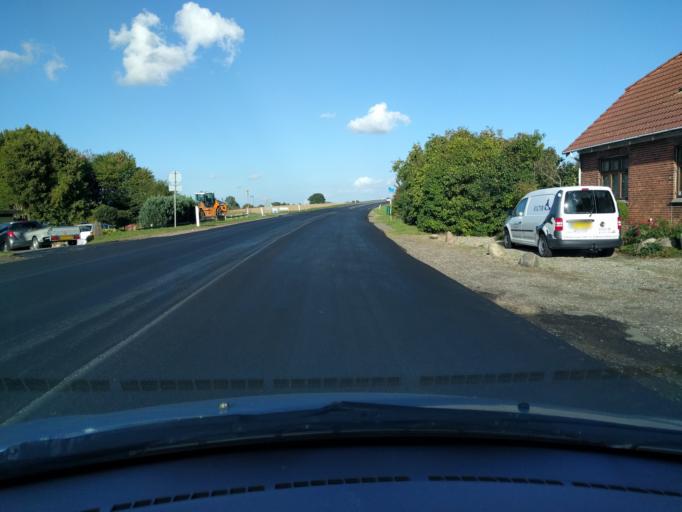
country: DK
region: South Denmark
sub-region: Assens Kommune
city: Glamsbjerg
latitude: 55.2739
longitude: 10.1406
